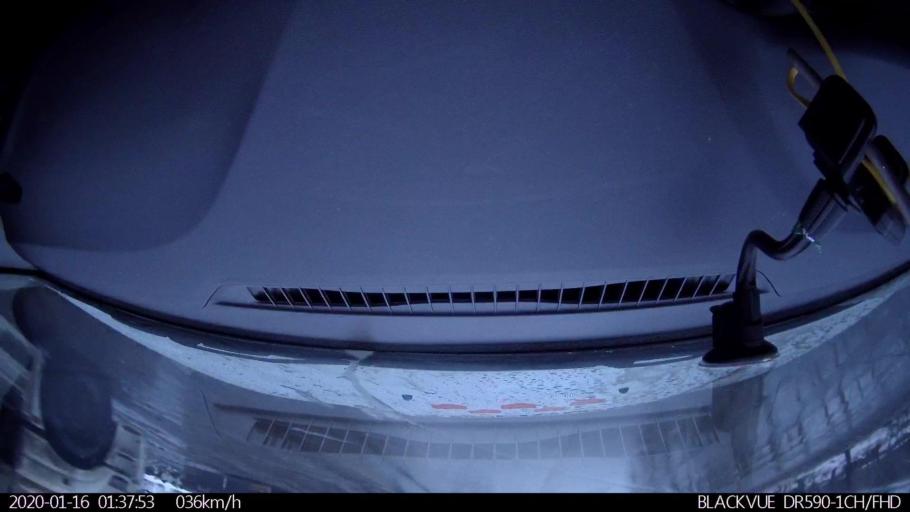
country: RU
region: Nizjnij Novgorod
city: Gorbatovka
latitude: 56.3392
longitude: 43.8046
